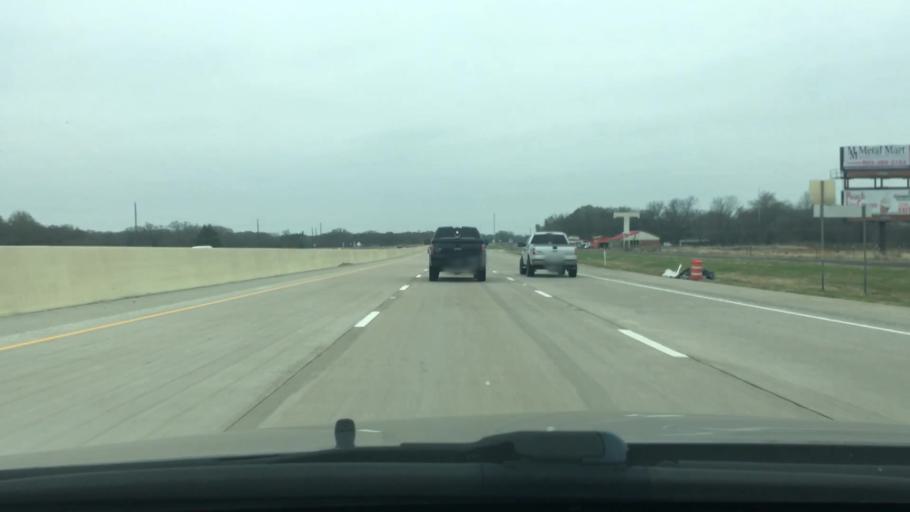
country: US
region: Texas
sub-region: Navarro County
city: Corsicana
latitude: 31.9688
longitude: -96.4218
